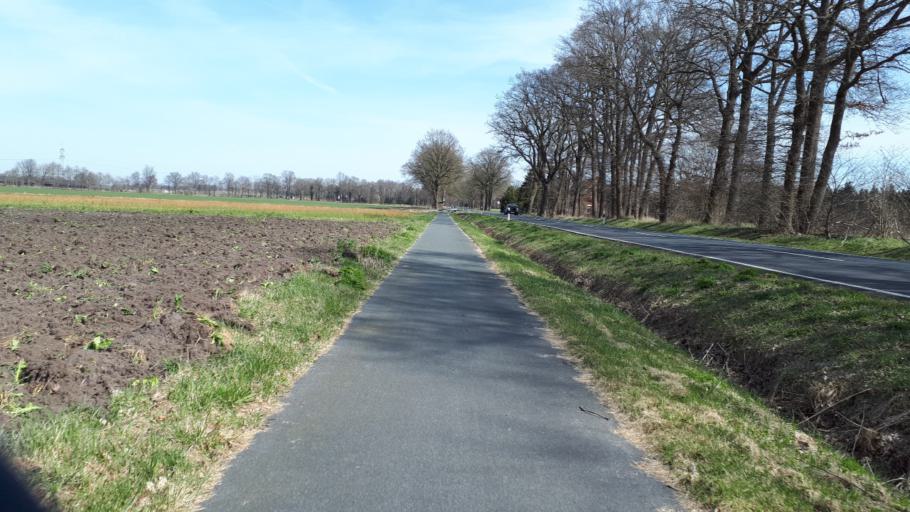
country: DE
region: Lower Saxony
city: Garrel
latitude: 52.9700
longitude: 8.0497
